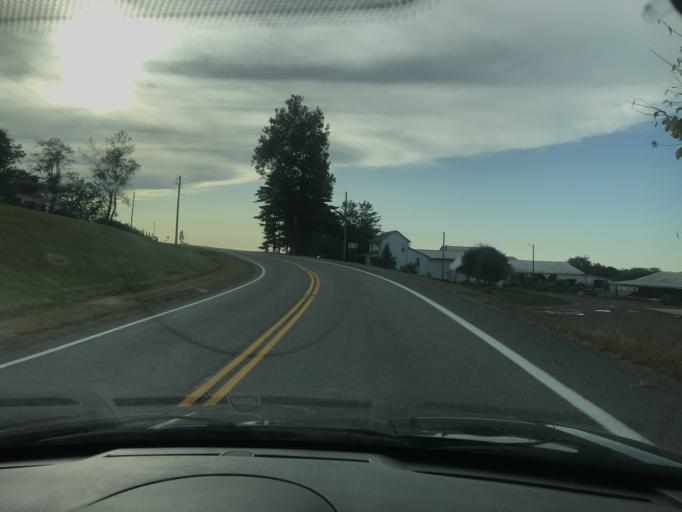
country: US
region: Ohio
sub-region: Logan County
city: West Liberty
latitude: 40.2672
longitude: -83.6825
